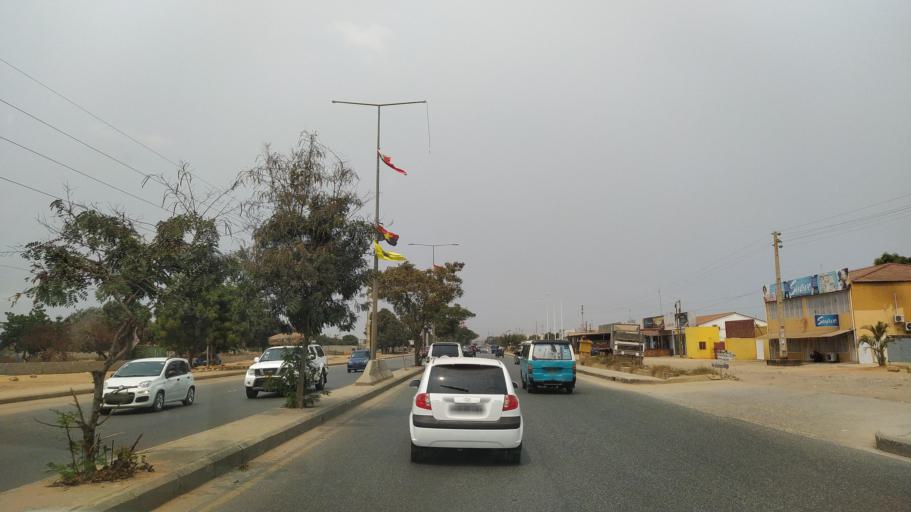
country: AO
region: Luanda
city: Luanda
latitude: -8.9935
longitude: 13.3972
